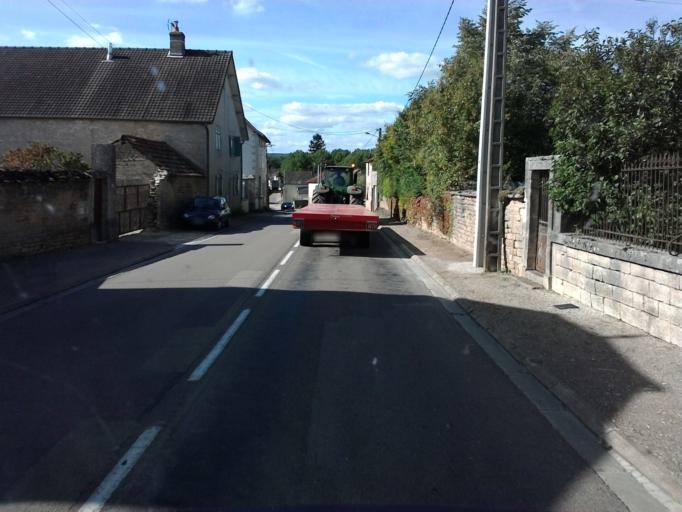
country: FR
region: Bourgogne
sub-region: Departement de la Cote-d'Or
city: Chatillon-sur-Seine
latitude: 47.9151
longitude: 4.6682
